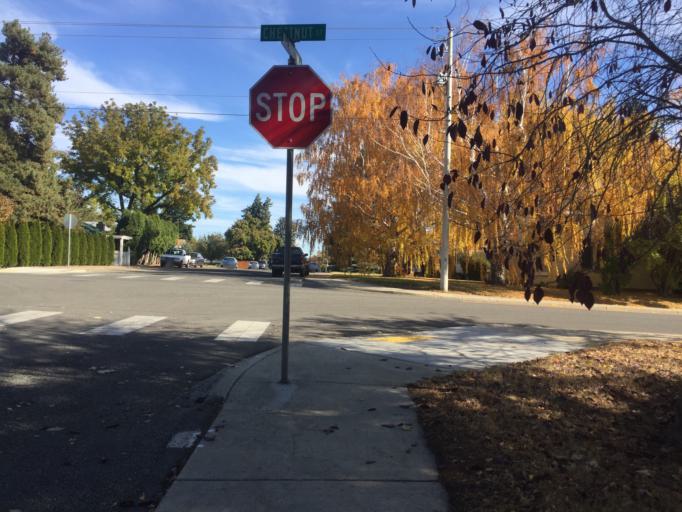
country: US
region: Washington
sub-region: Kittitas County
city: Ellensburg
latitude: 46.9904
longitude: -120.5373
